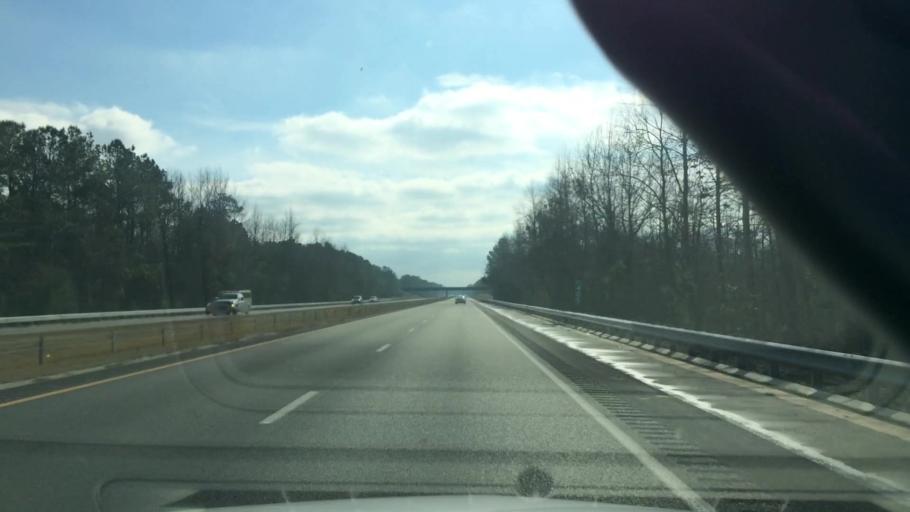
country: US
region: North Carolina
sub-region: Pender County
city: Rocky Point
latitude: 34.4852
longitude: -77.8783
